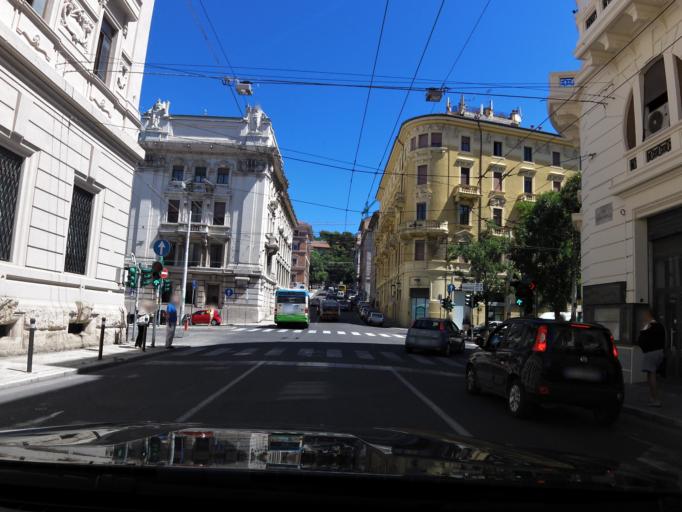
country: IT
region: The Marches
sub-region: Provincia di Ancona
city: Le Grazie di Ancona
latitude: 43.6161
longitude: 13.5191
